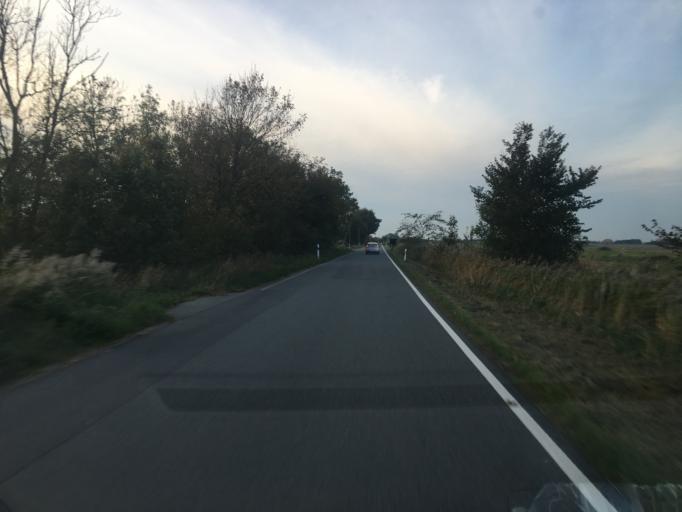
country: DE
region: Schleswig-Holstein
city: Aventoft
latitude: 54.8991
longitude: 8.8450
